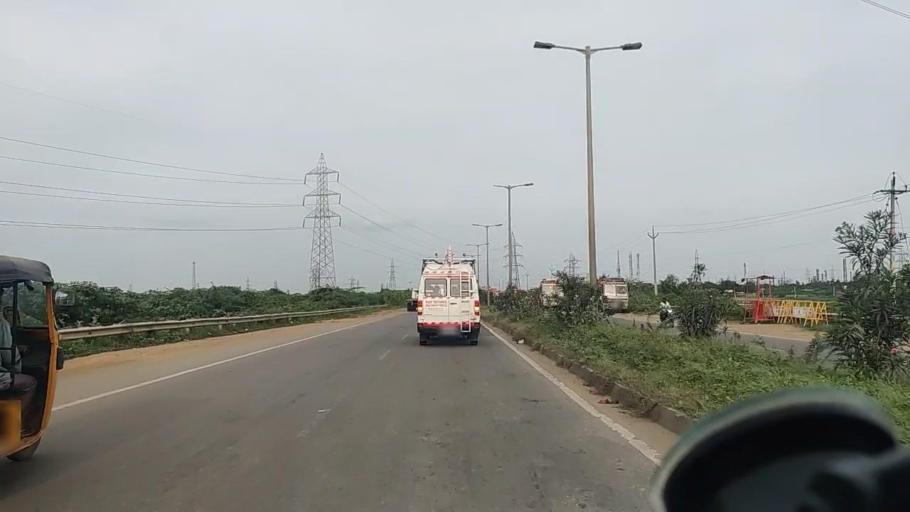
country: IN
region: Tamil Nadu
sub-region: Thiruvallur
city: Manali
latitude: 13.1815
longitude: 80.2647
